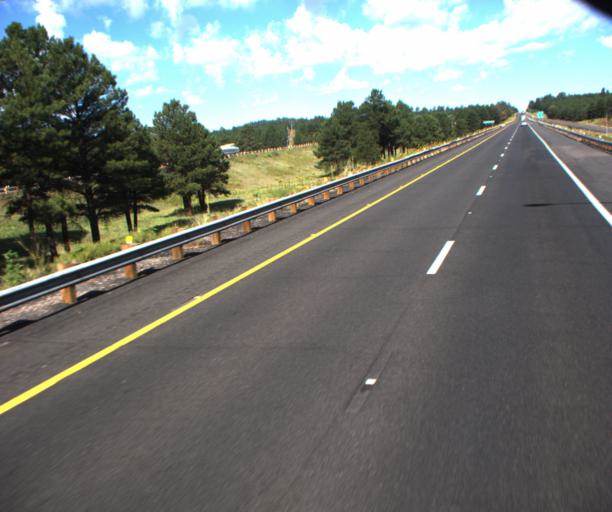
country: US
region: Arizona
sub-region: Coconino County
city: Flagstaff
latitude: 35.1852
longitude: -111.7070
